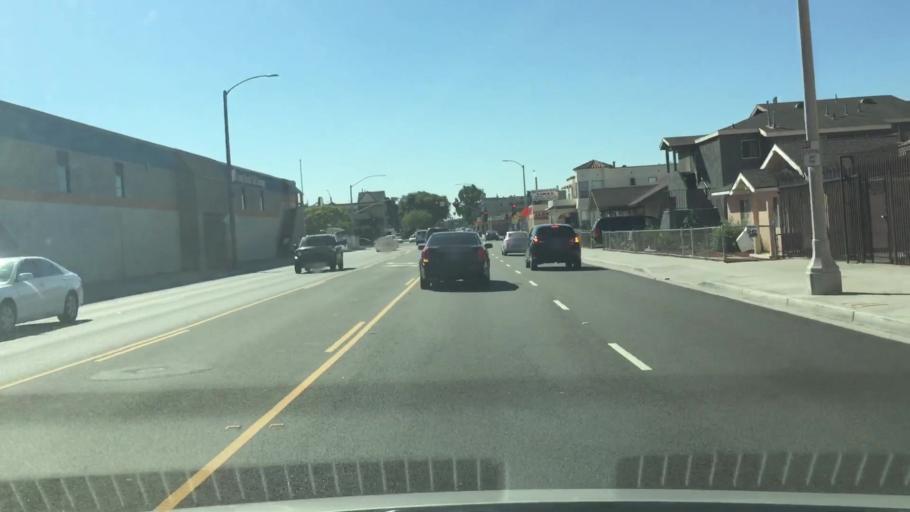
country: US
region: California
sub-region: Los Angeles County
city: Signal Hill
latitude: 33.7912
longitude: -118.1677
